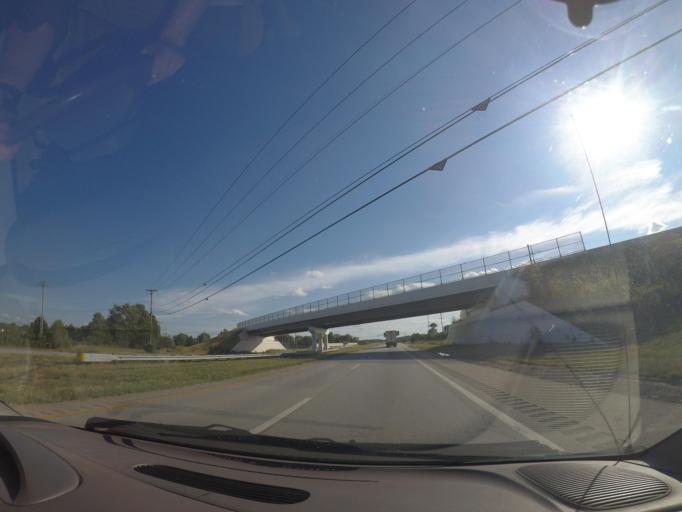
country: US
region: Ohio
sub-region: Henry County
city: Napoleon
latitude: 41.4018
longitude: -84.1410
